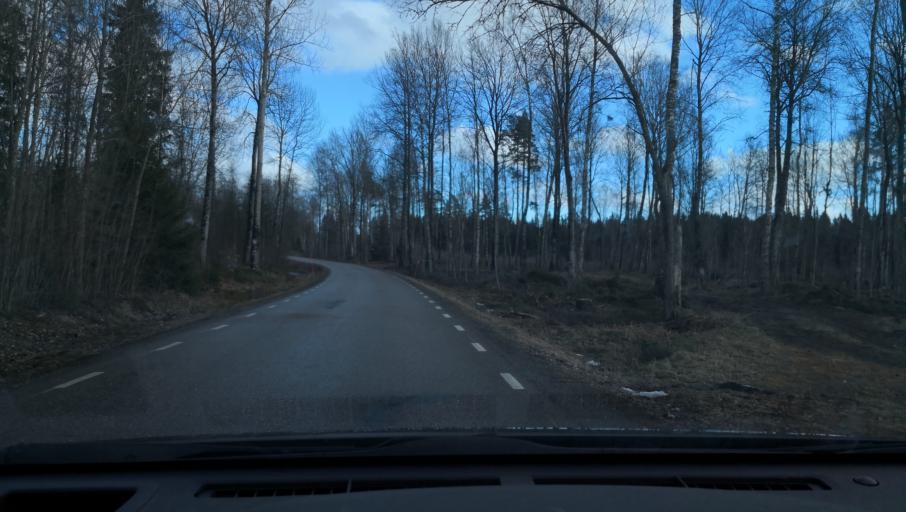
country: SE
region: OErebro
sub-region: Lindesbergs Kommun
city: Fellingsbro
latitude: 59.3398
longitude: 15.6918
